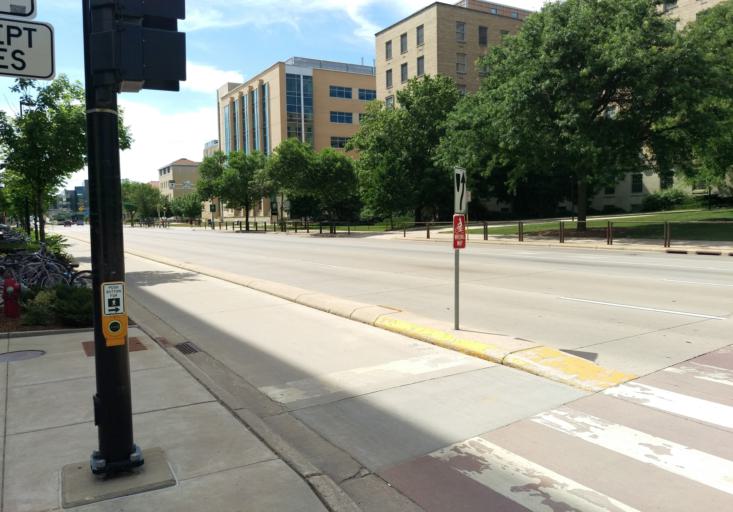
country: US
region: Wisconsin
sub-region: Dane County
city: Madison
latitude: 43.0732
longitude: -89.4074
